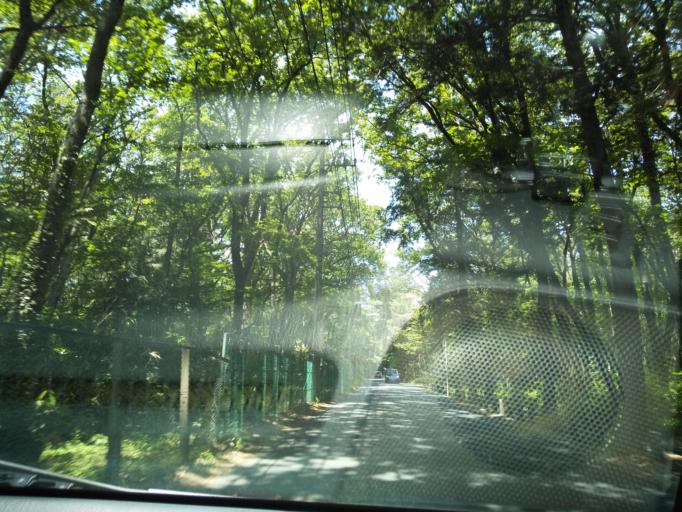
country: JP
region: Tokyo
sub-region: Machida-shi
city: Machida
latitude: 35.5414
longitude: 139.4113
